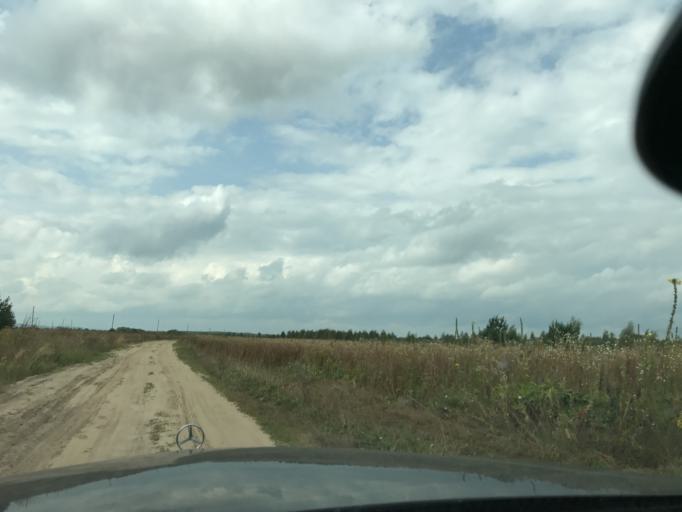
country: RU
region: Nizjnij Novgorod
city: Vacha
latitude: 55.9818
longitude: 42.7877
